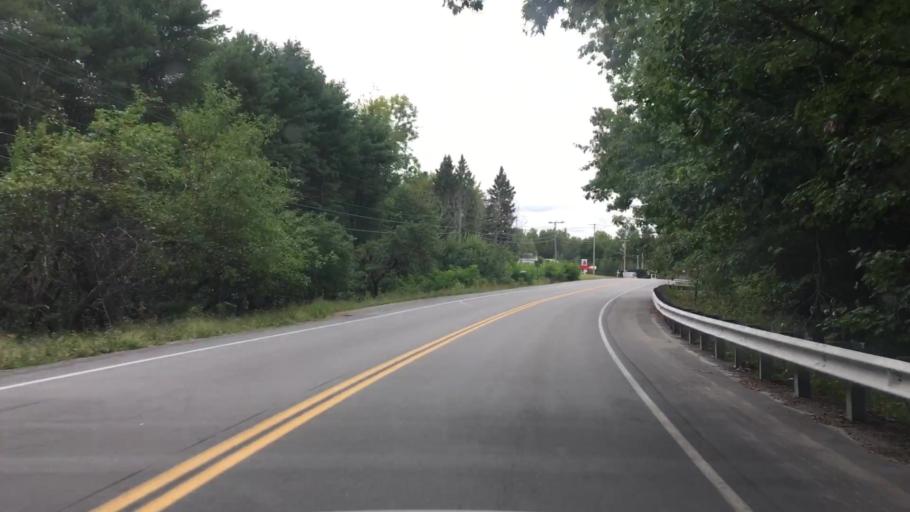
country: US
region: Maine
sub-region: Penobscot County
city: Milford
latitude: 44.9552
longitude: -68.6980
